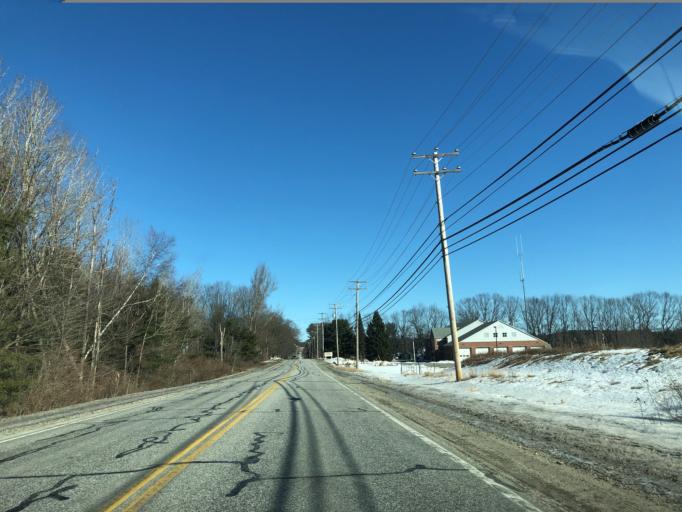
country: US
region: Maine
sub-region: Cumberland County
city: South Windham
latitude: 43.7779
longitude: -70.4165
